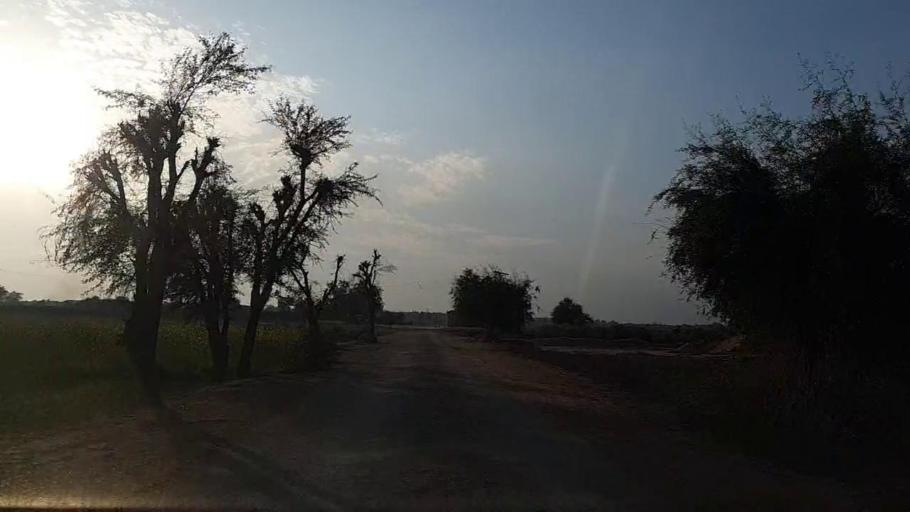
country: PK
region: Sindh
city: Jam Sahib
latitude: 26.3945
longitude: 68.5097
